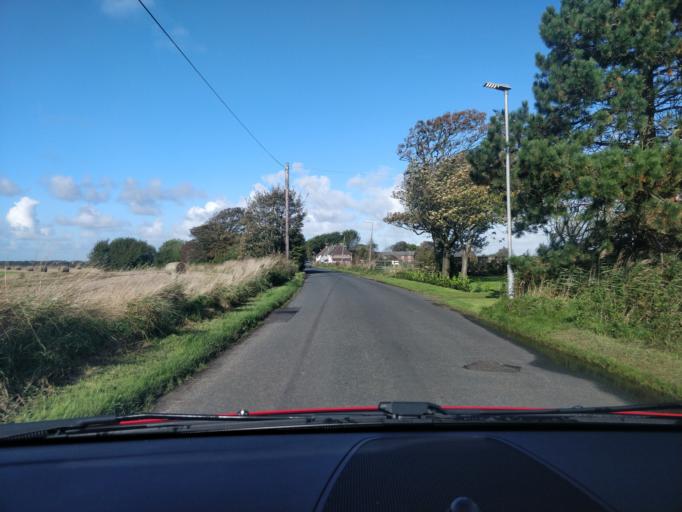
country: GB
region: England
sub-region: Lancashire
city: Banks
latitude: 53.6230
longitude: -2.9390
